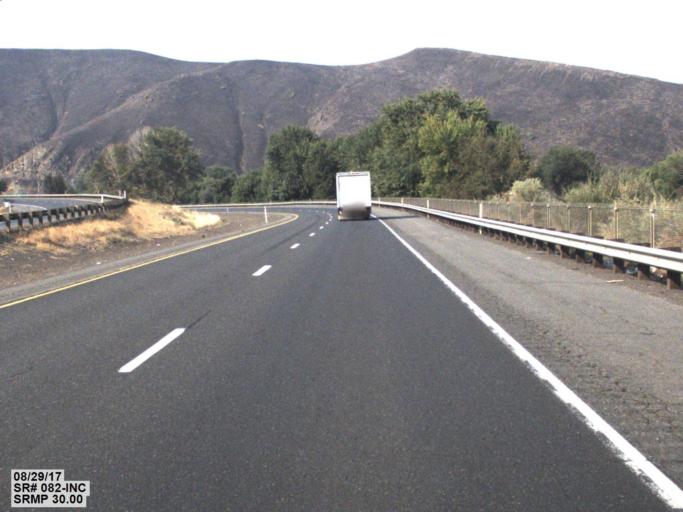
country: US
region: Washington
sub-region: Yakima County
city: Selah
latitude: 46.6399
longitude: -120.5205
